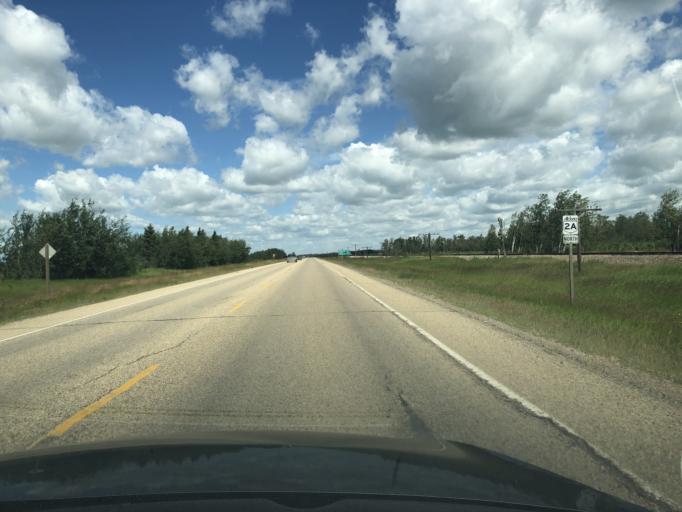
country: CA
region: Alberta
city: Millet
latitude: 53.1006
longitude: -113.4739
